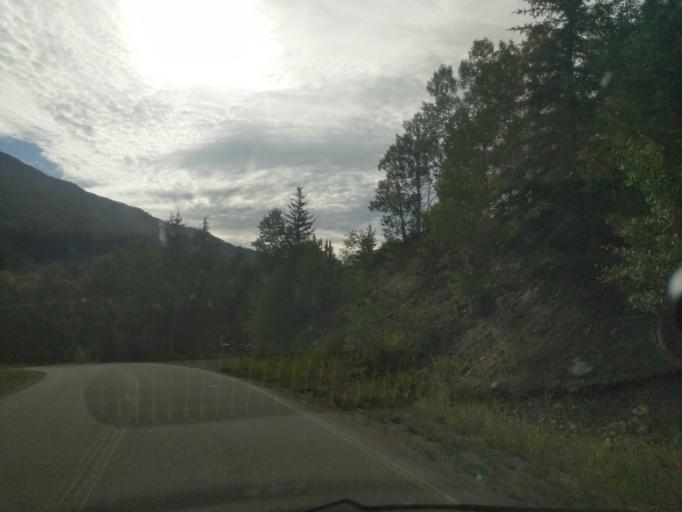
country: US
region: Colorado
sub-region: Garfield County
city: Carbondale
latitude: 39.0849
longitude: -107.2442
